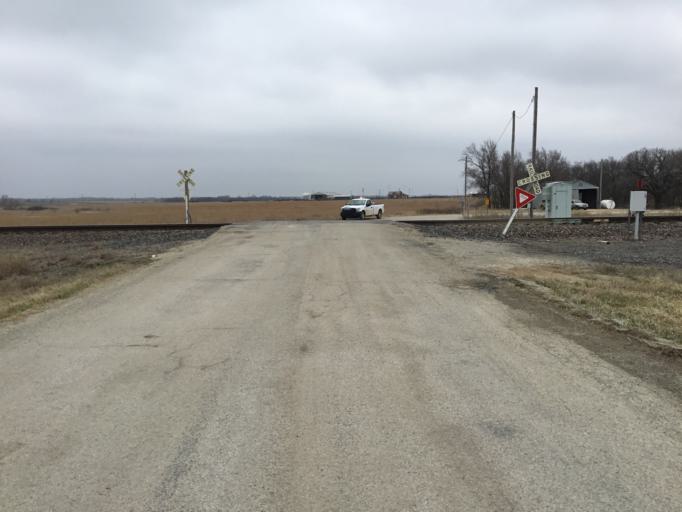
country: US
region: Kansas
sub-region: Dickinson County
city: Herington
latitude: 38.7356
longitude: -96.8470
